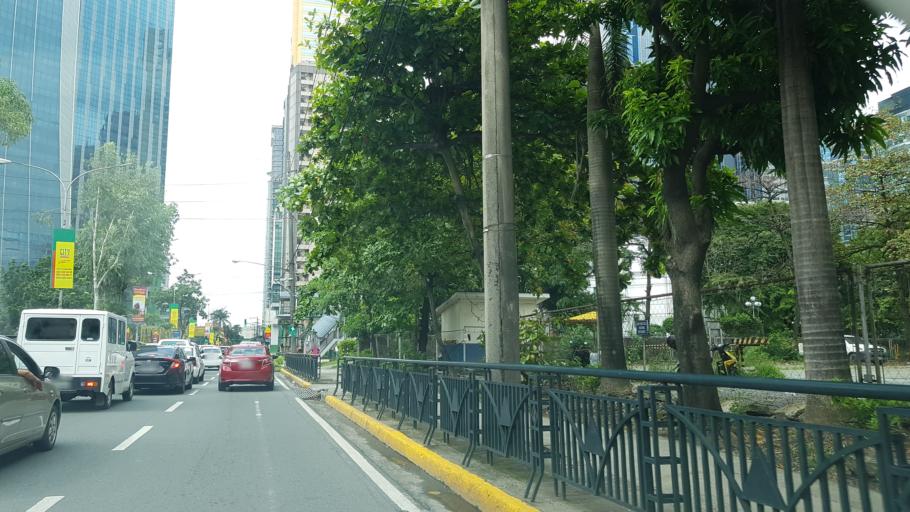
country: PH
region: Metro Manila
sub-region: Pasig
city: Pasig City
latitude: 14.5832
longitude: 121.0601
